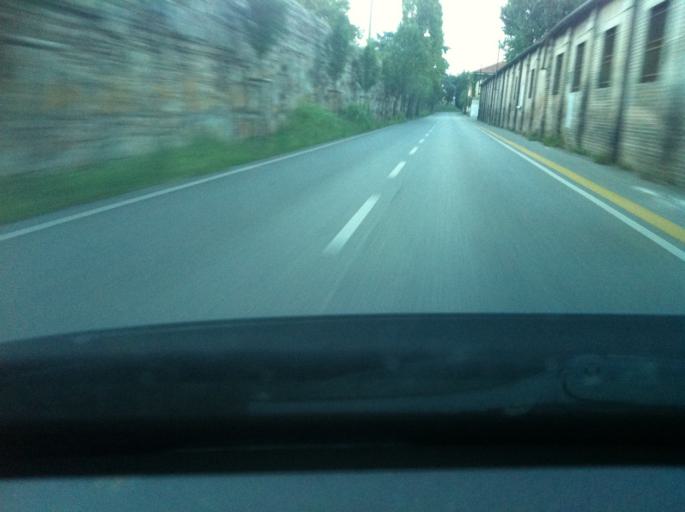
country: IT
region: Veneto
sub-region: Provincia di Padova
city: Padova
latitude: 45.4095
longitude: 11.8644
